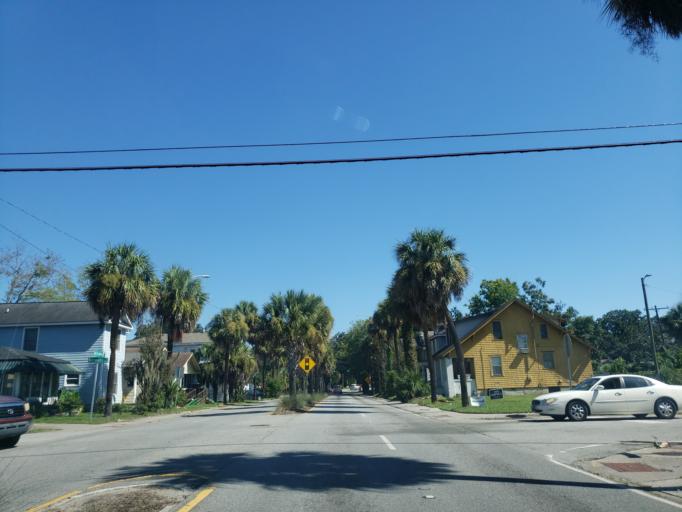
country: US
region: Georgia
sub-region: Chatham County
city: Savannah
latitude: 32.0543
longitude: -81.1085
